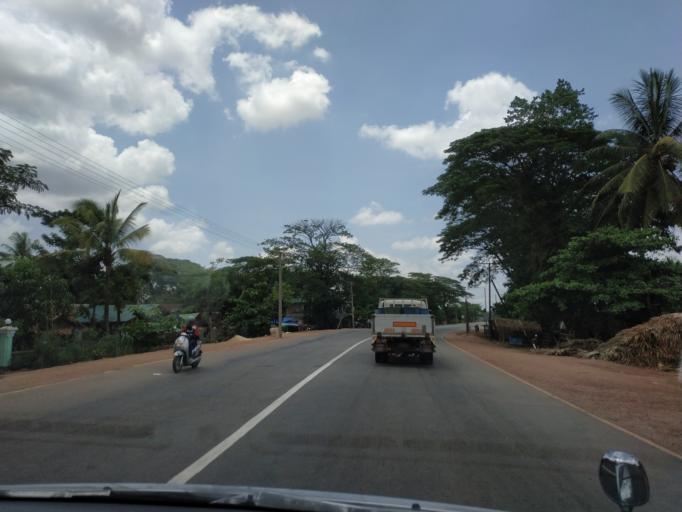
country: MM
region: Bago
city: Bago
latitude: 17.4668
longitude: 96.5836
